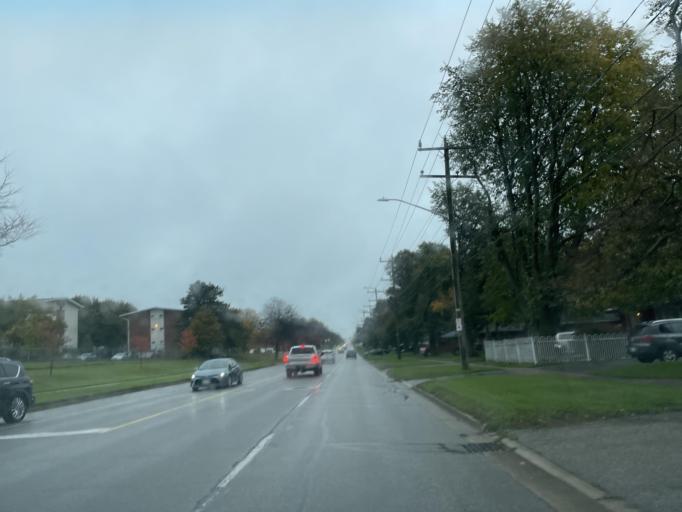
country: CA
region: Ontario
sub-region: Wellington County
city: Guelph
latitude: 43.5760
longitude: -80.2576
